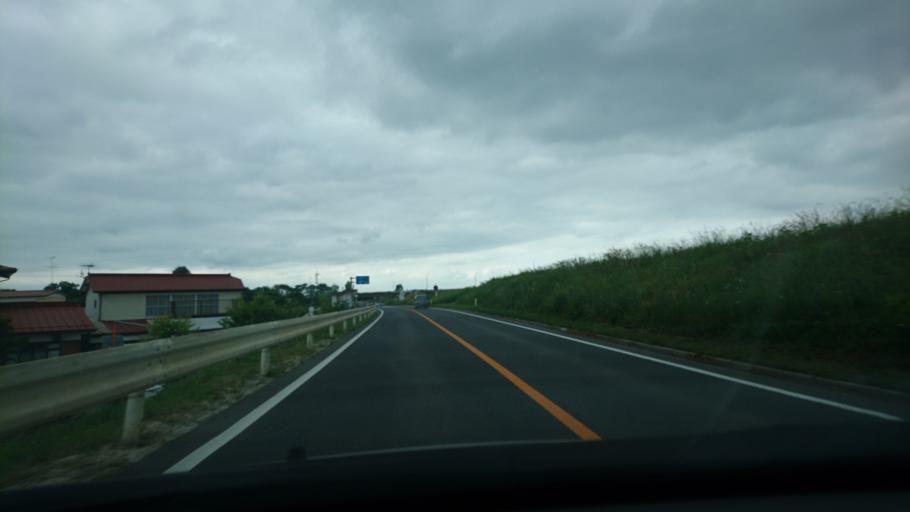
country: JP
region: Iwate
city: Ichinoseki
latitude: 38.7413
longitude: 141.1513
